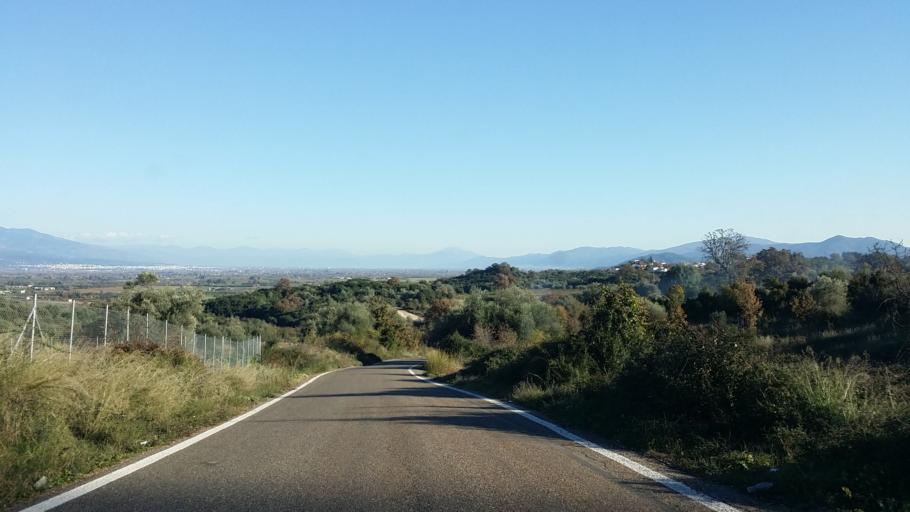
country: GR
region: West Greece
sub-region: Nomos Aitolias kai Akarnanias
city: Fitiai
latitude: 38.6240
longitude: 21.2076
